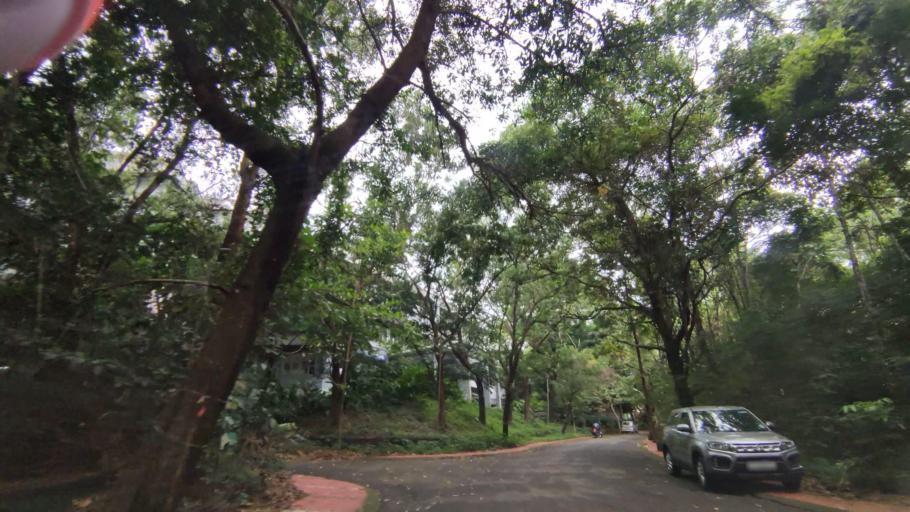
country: IN
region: Kerala
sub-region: Kottayam
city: Kottayam
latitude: 9.6602
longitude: 76.5325
